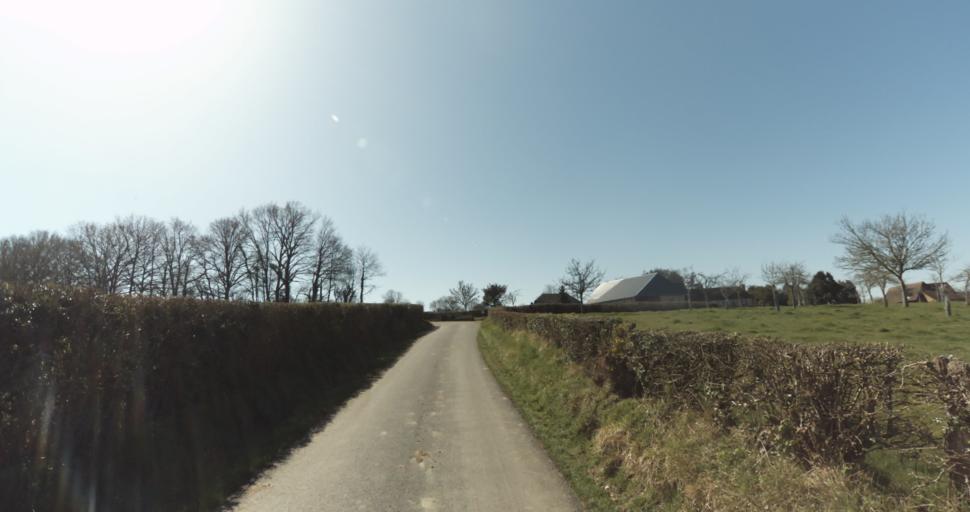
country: FR
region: Lower Normandy
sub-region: Departement du Calvados
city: Livarot
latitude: 49.0101
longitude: 0.0817
